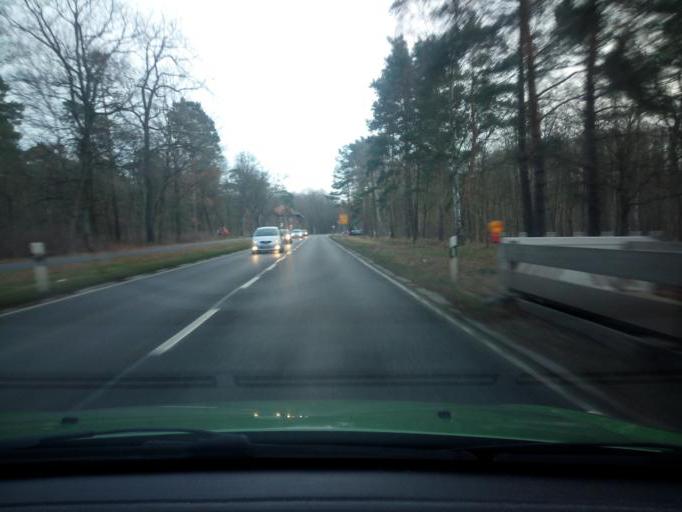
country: DE
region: Berlin
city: Friedrichshagen
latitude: 52.4314
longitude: 13.6121
